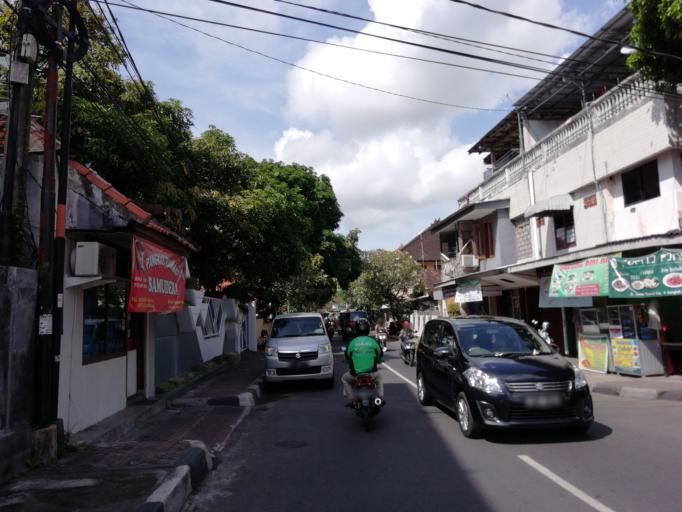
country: ID
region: Bali
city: Denpasar
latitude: -8.6738
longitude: 115.2162
